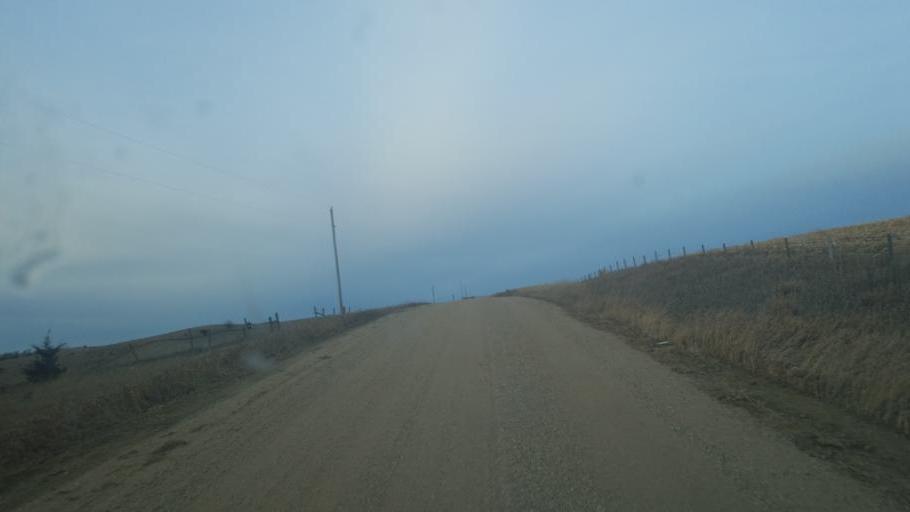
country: US
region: Nebraska
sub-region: Knox County
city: Center
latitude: 42.7198
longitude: -97.7793
